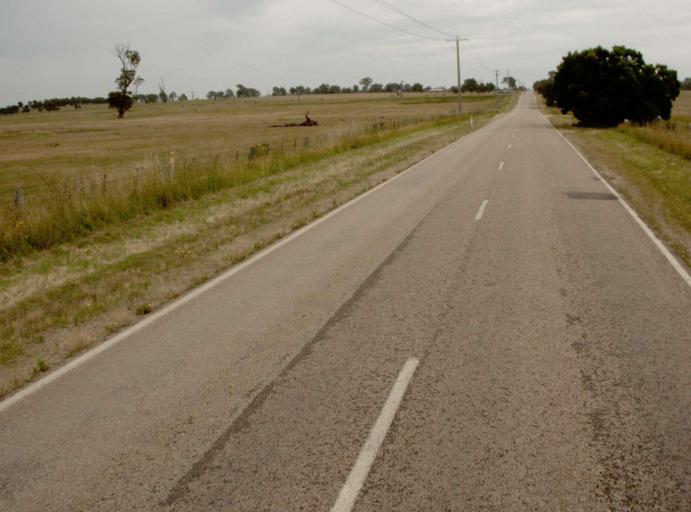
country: AU
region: Victoria
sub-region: East Gippsland
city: Bairnsdale
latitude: -37.8062
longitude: 147.4384
